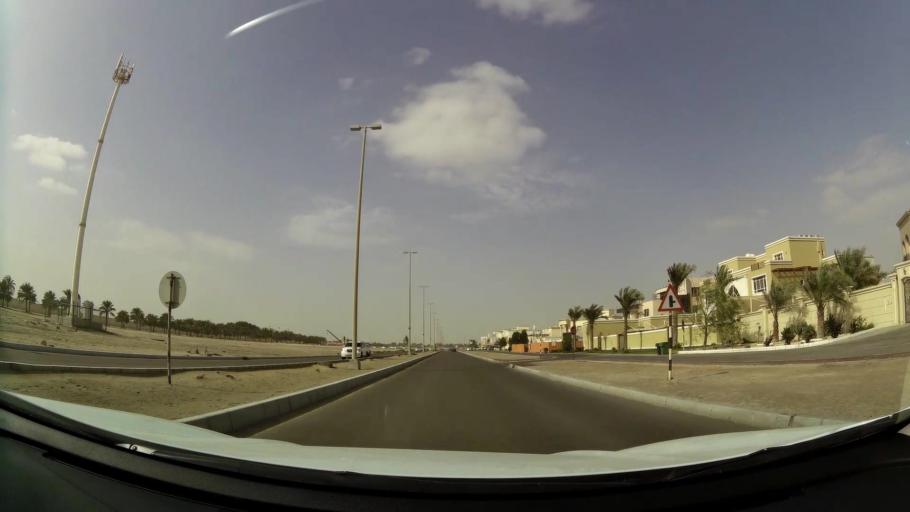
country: AE
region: Abu Dhabi
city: Abu Dhabi
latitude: 24.4205
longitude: 54.5468
